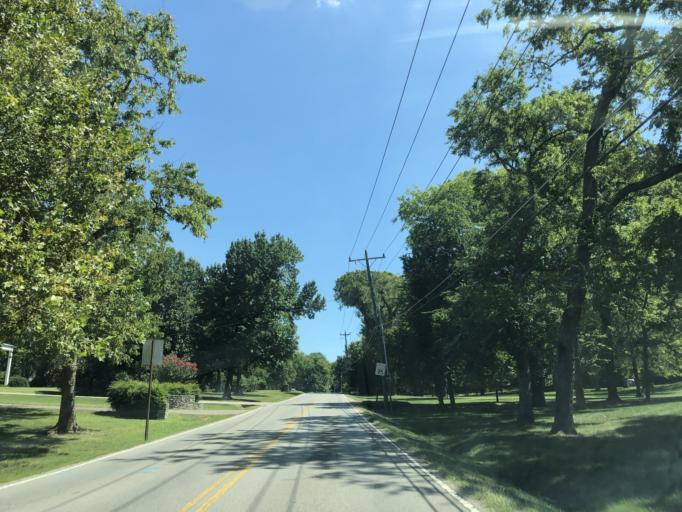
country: US
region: Tennessee
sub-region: Davidson County
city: Oak Hill
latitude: 36.0808
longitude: -86.8025
